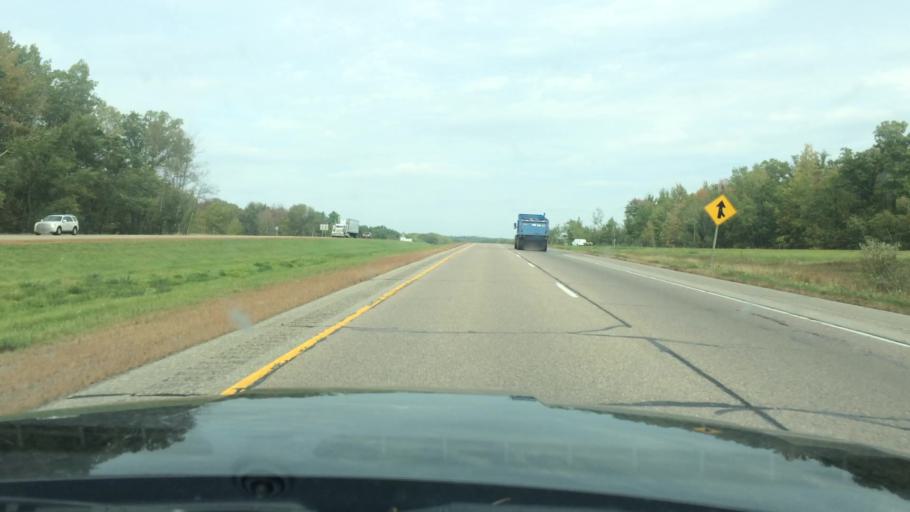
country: US
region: Wisconsin
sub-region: Marathon County
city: Mosinee
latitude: 44.6765
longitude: -89.6417
